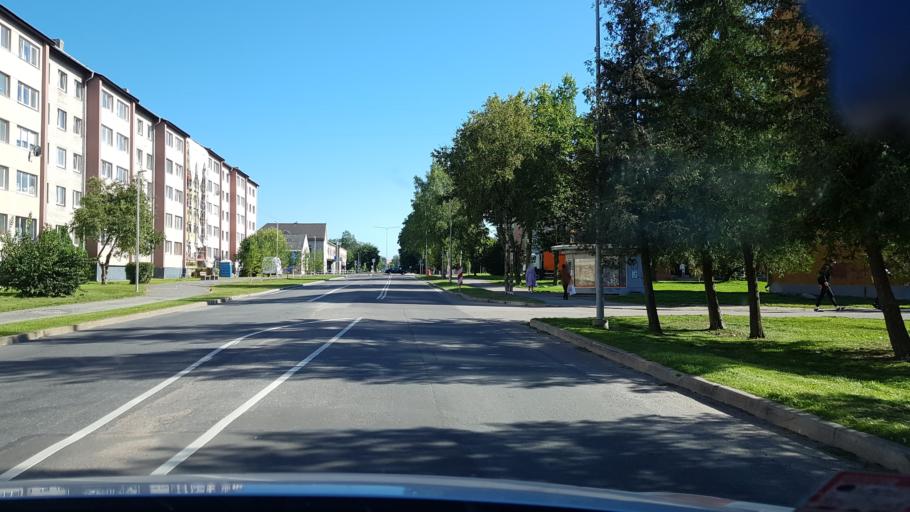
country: EE
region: Ida-Virumaa
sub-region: Kohtla-Jaerve linn
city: Kohtla-Jarve
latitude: 59.4055
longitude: 27.2837
